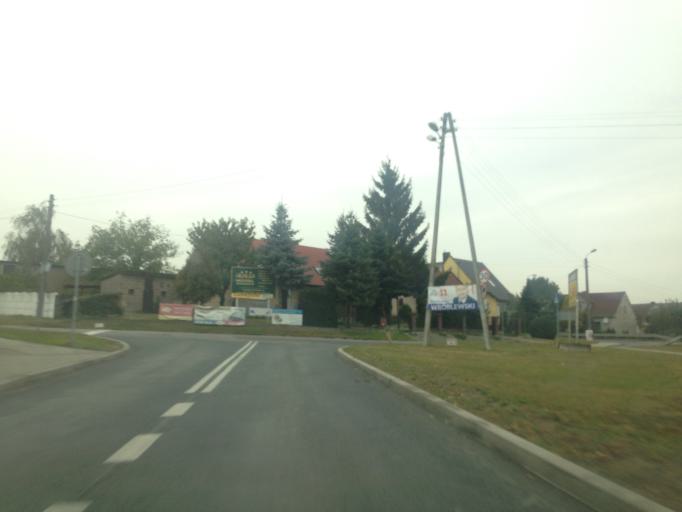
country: PL
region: Greater Poland Voivodeship
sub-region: Powiat poznanski
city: Swarzedz
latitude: 52.3429
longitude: 17.0761
